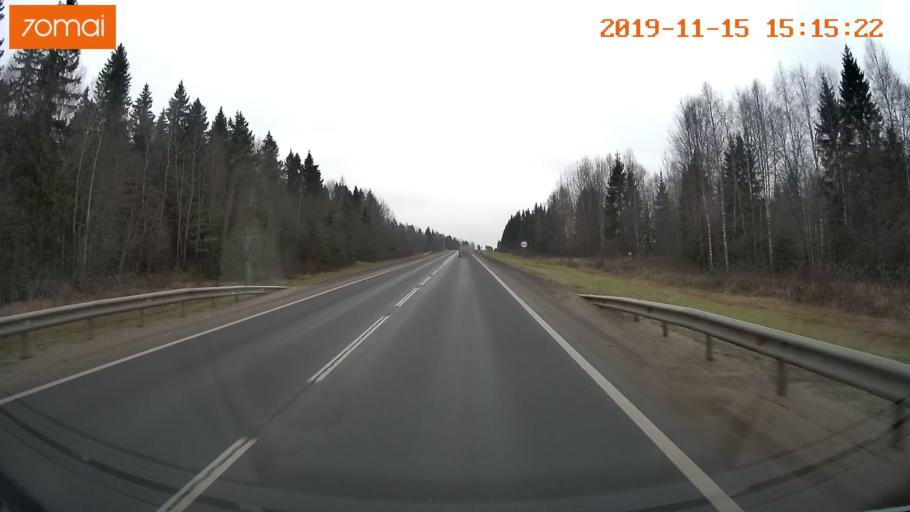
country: RU
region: Jaroslavl
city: Danilov
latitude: 58.2857
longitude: 40.1994
